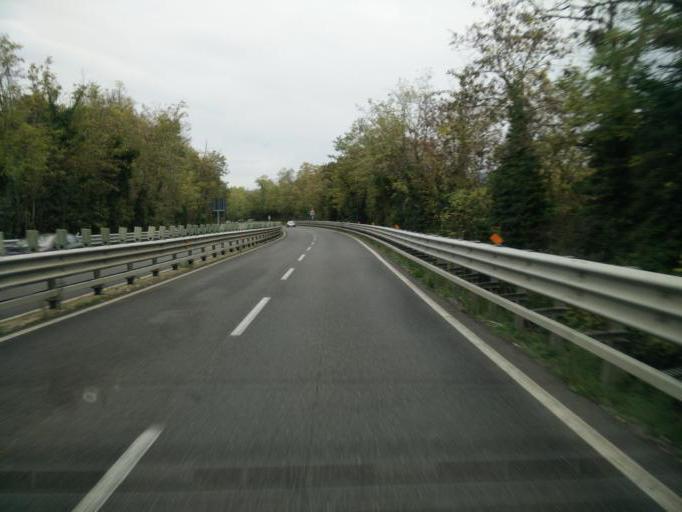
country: IT
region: Tuscany
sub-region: Province of Florence
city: Sambuca
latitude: 43.5570
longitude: 11.2115
